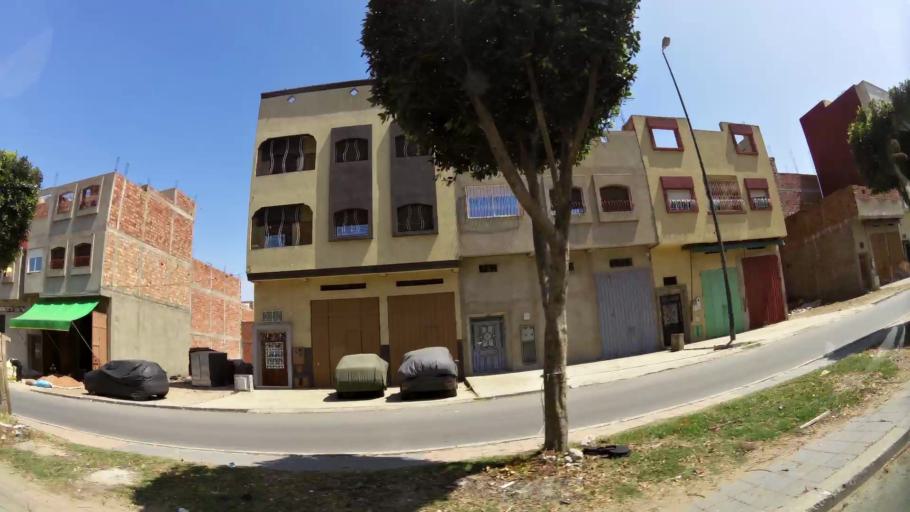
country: MA
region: Gharb-Chrarda-Beni Hssen
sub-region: Kenitra Province
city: Kenitra
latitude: 34.2426
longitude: -6.5442
